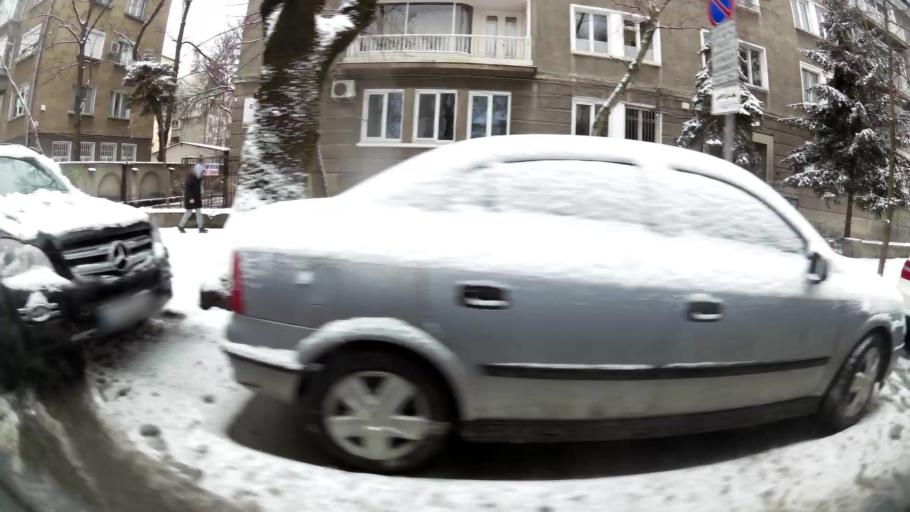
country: BG
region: Sofia-Capital
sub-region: Stolichna Obshtina
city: Sofia
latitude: 42.6945
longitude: 23.3434
